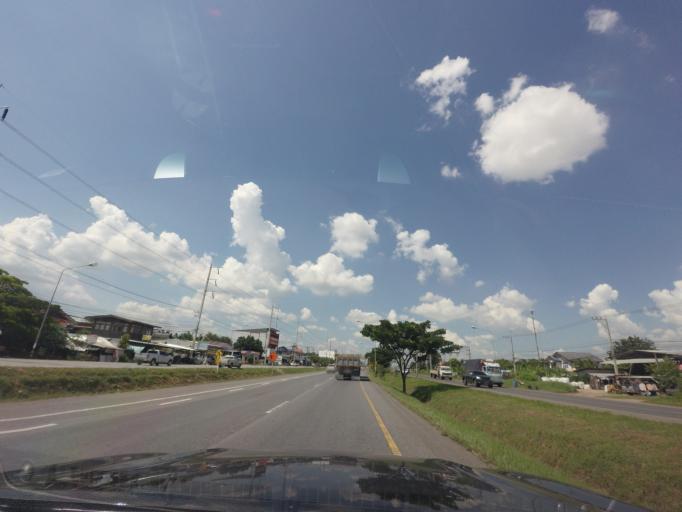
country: TH
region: Nakhon Ratchasima
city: Nakhon Ratchasima
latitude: 14.9743
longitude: 102.0519
